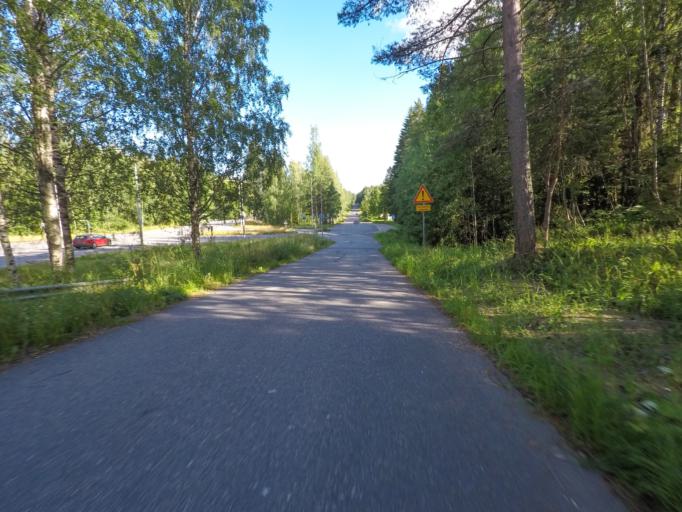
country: FI
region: South Karelia
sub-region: Lappeenranta
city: Lappeenranta
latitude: 61.0894
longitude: 28.1424
